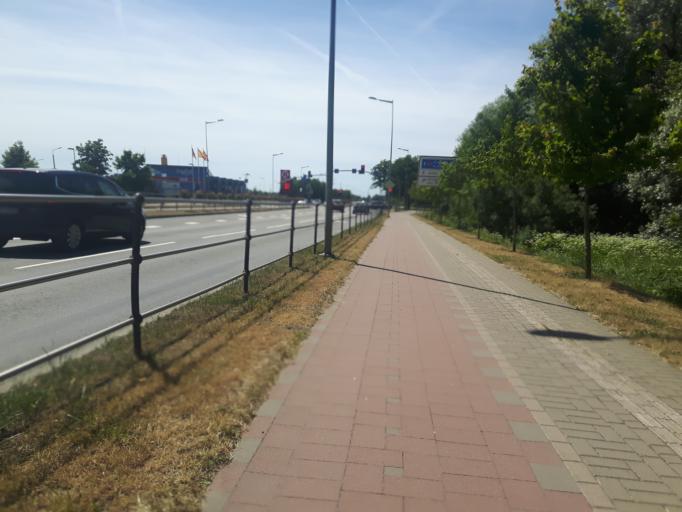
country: LV
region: Liepaja
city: Vec-Liepaja
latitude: 56.5354
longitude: 21.0575
